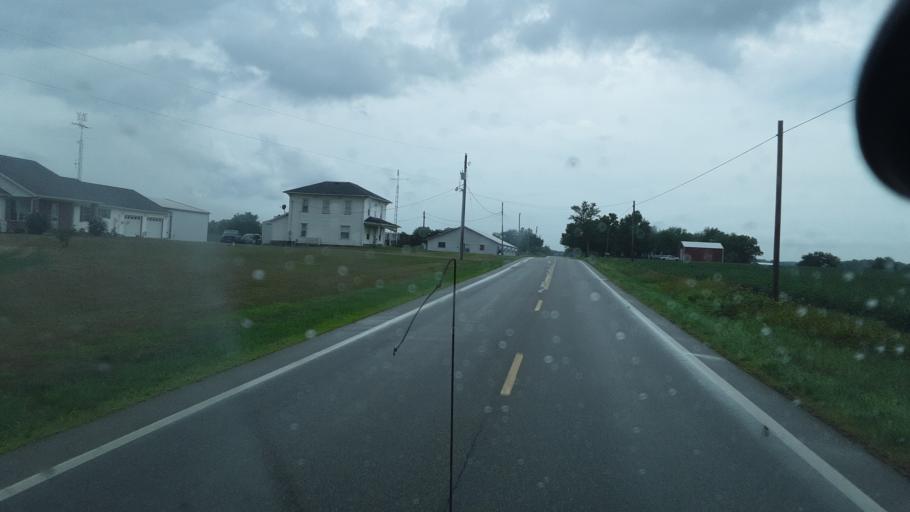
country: US
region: Ohio
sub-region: Williams County
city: Edgerton
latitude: 41.5563
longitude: -84.7886
